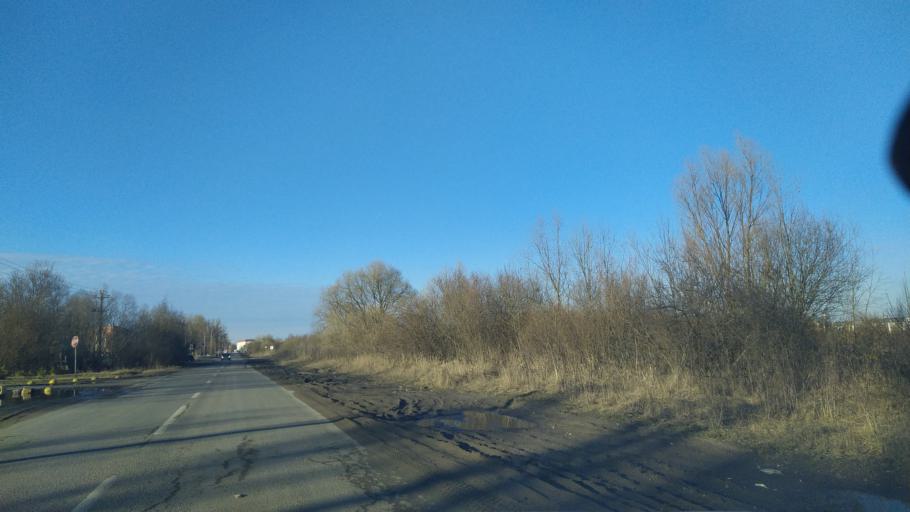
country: RU
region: St.-Petersburg
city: Pushkin
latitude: 59.6937
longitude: 30.3962
